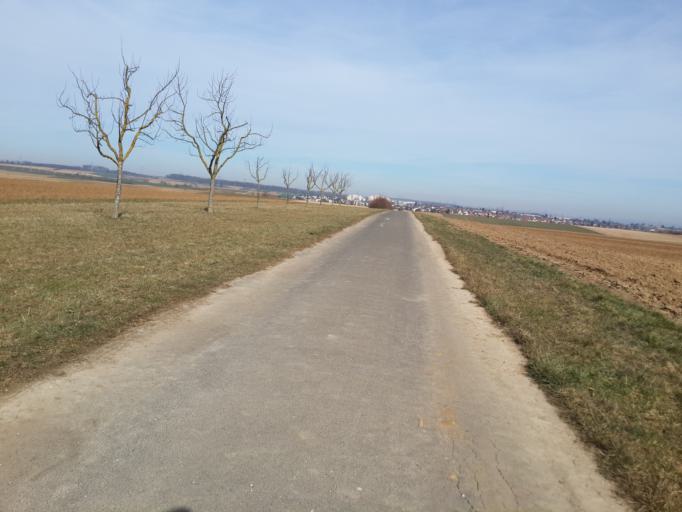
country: DE
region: Baden-Wuerttemberg
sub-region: Regierungsbezirk Stuttgart
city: Leingarten
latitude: 49.1461
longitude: 9.1671
